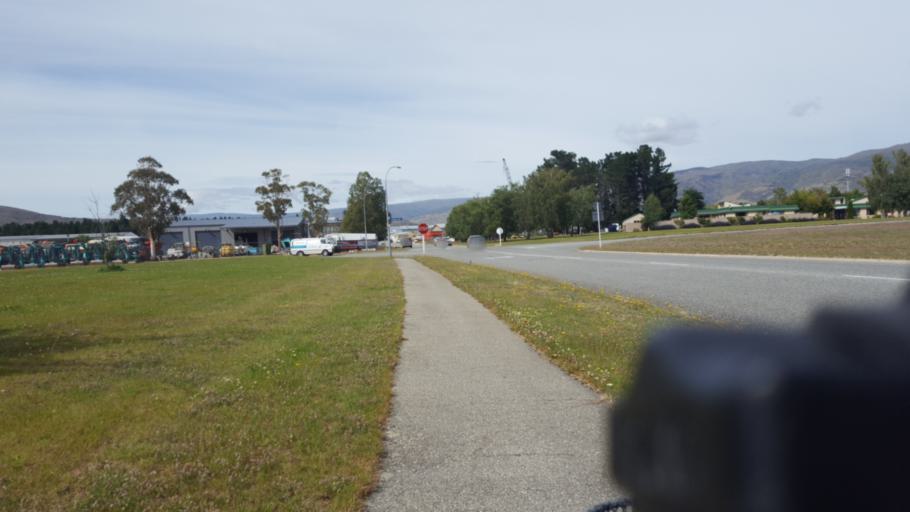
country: NZ
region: Otago
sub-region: Queenstown-Lakes District
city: Wanaka
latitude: -45.0486
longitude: 169.1848
